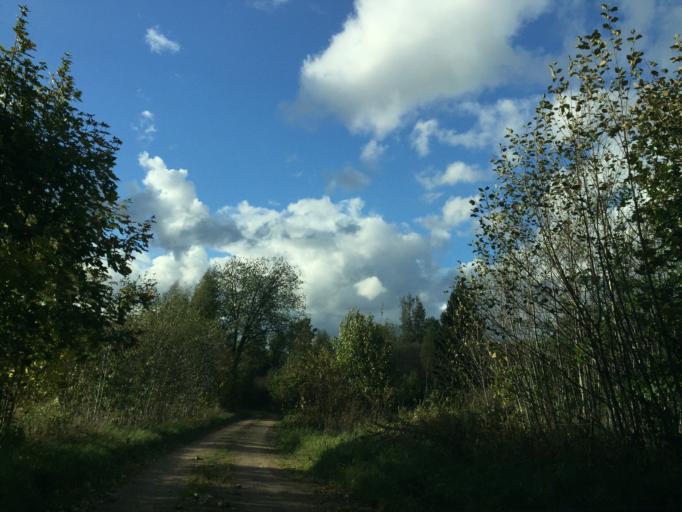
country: LV
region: Ligatne
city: Ligatne
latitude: 57.1243
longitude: 25.1301
